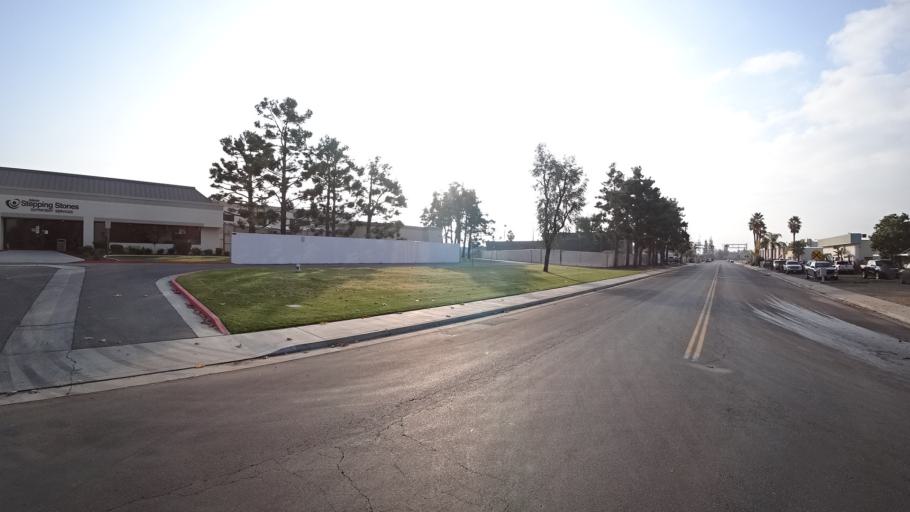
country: US
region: California
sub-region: Kern County
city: Bakersfield
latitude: 35.3165
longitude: -119.0614
